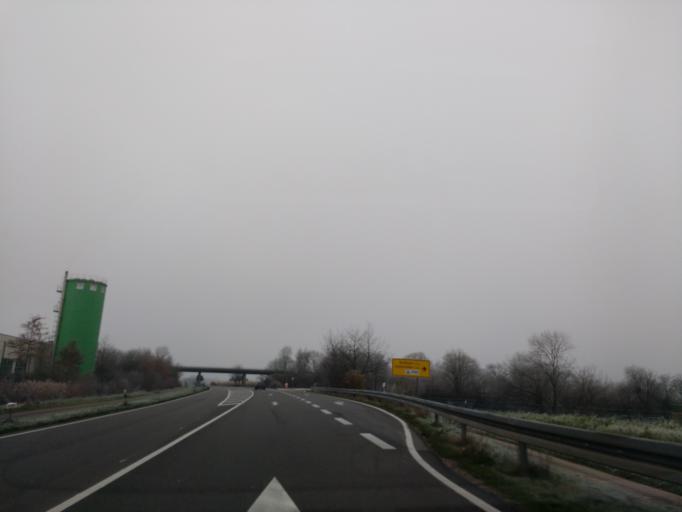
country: DE
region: Baden-Wuerttemberg
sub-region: Freiburg Region
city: Appenweier
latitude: 48.5407
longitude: 8.0220
